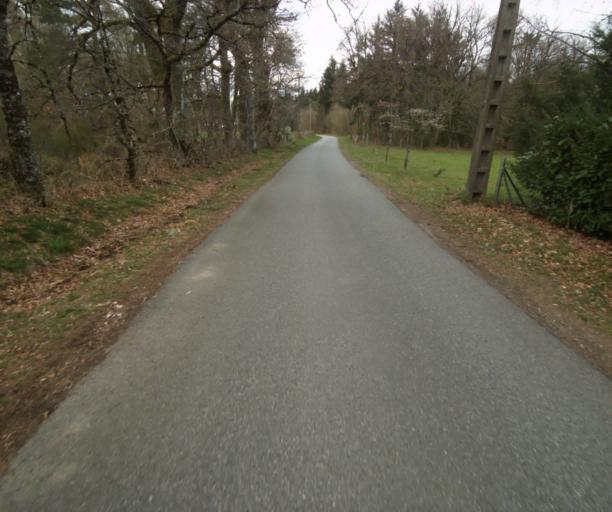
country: FR
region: Limousin
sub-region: Departement de la Correze
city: Correze
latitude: 45.2976
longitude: 1.9215
